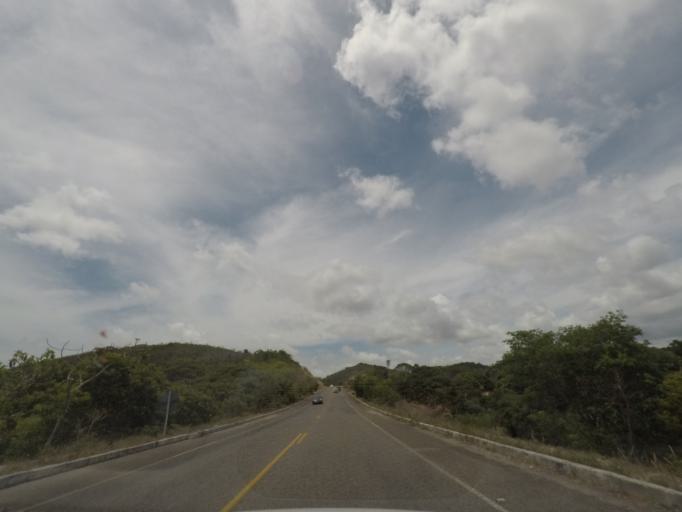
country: BR
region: Bahia
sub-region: Conde
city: Conde
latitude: -11.7188
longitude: -37.5736
